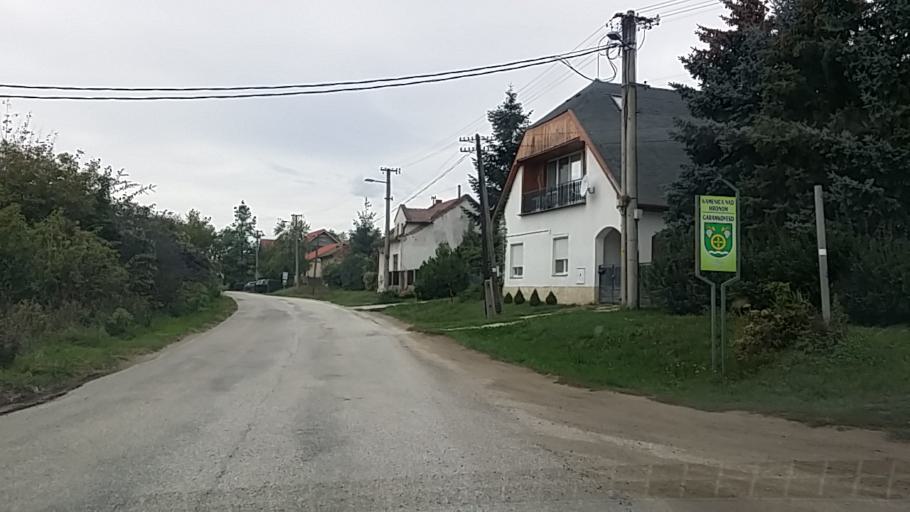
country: HU
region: Komarom-Esztergom
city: Esztergom
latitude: 47.8251
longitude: 18.7457
